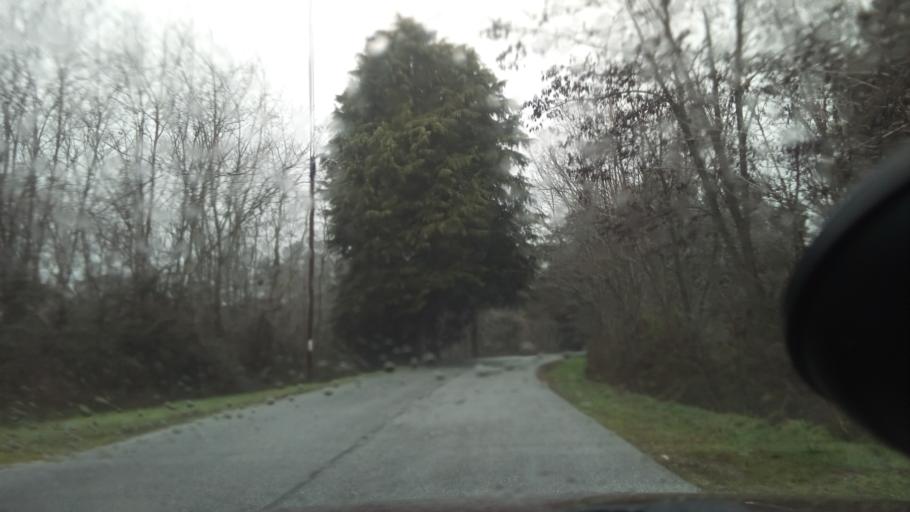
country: PT
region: Guarda
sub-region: Fornos de Algodres
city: Fornos de Algodres
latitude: 40.6075
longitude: -7.6374
